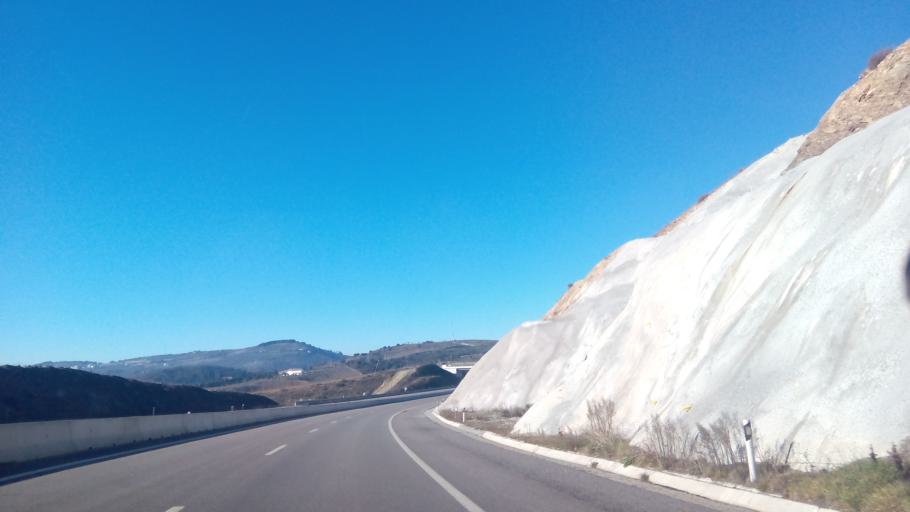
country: PT
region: Braganca
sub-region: Braganca Municipality
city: Braganca
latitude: 41.7819
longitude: -6.7026
